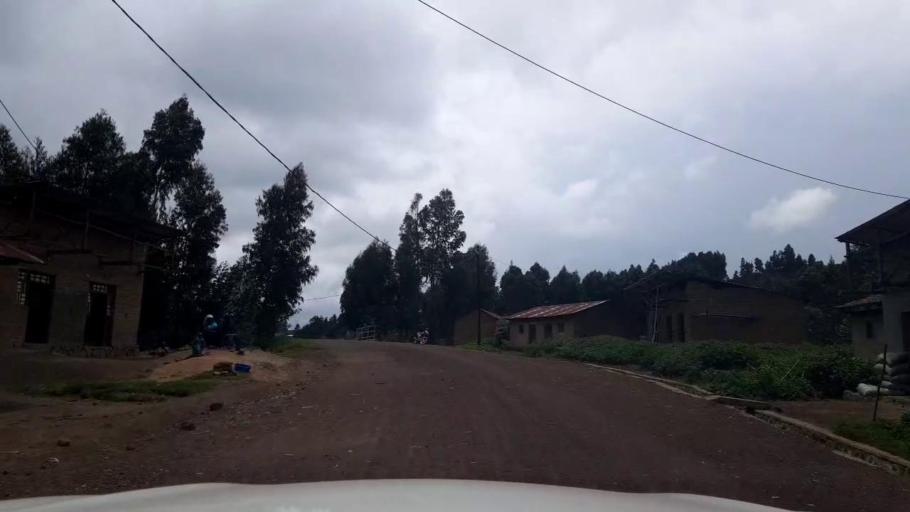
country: RW
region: Northern Province
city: Musanze
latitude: -1.5783
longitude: 29.4841
